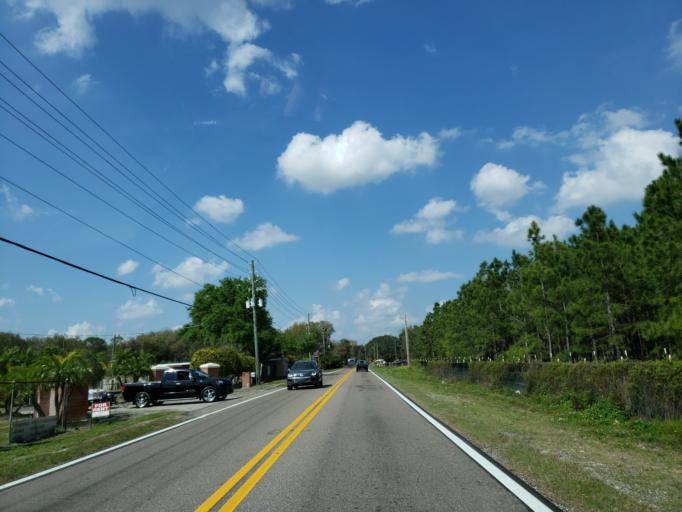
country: US
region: Florida
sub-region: Hillsborough County
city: Keystone
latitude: 28.1451
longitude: -82.5780
